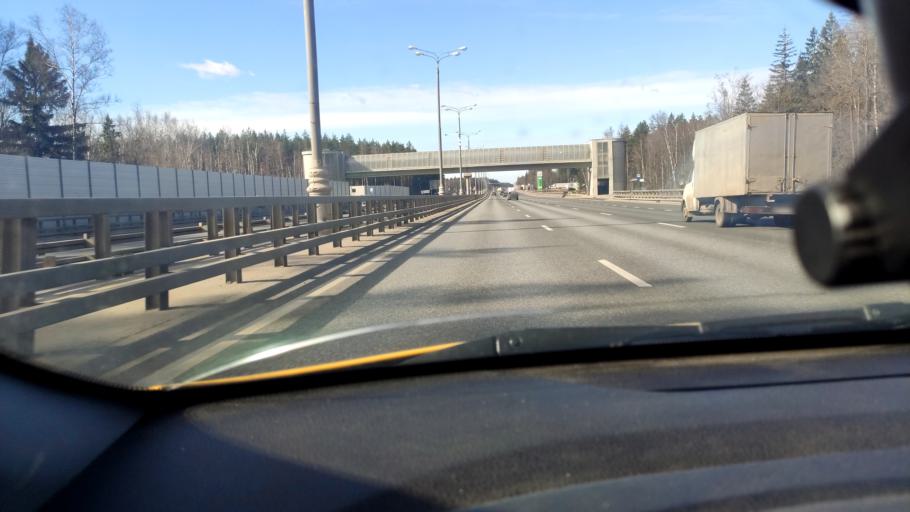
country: RU
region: Moskovskaya
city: Kokoshkino
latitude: 55.5535
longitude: 37.1397
